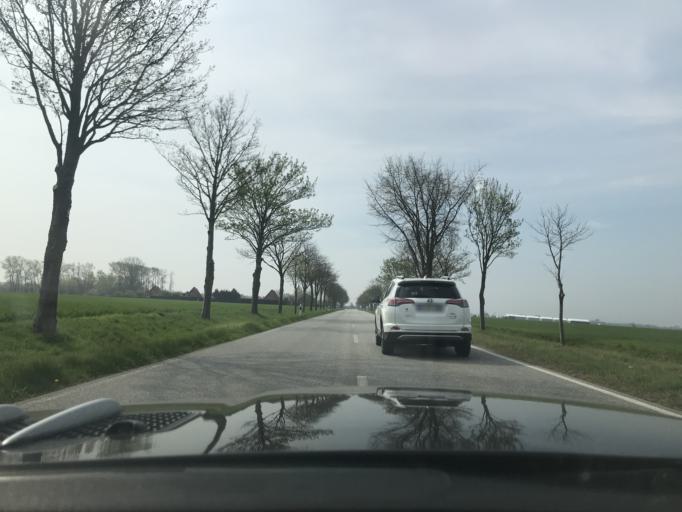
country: DE
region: Schleswig-Holstein
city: Grube
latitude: 54.2504
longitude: 11.0313
